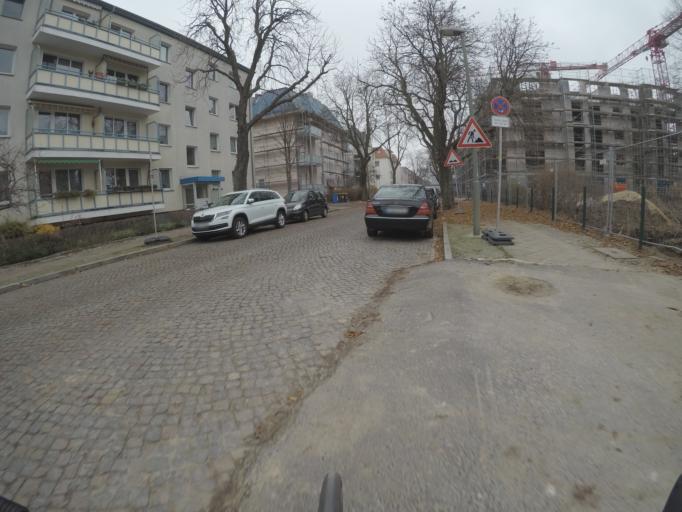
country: DE
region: Berlin
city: Oberschoneweide
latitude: 52.4591
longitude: 13.5343
